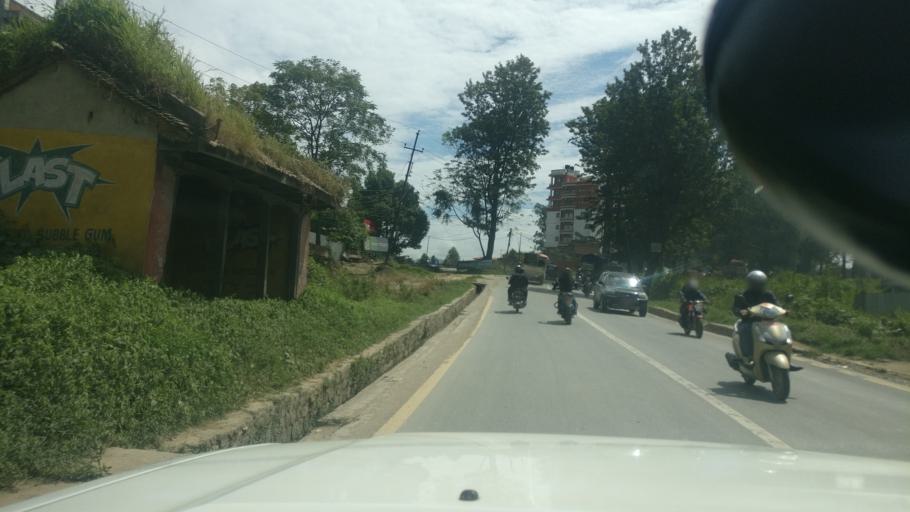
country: NP
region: Central Region
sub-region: Bagmati Zone
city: Bhaktapur
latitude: 27.6633
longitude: 85.4430
